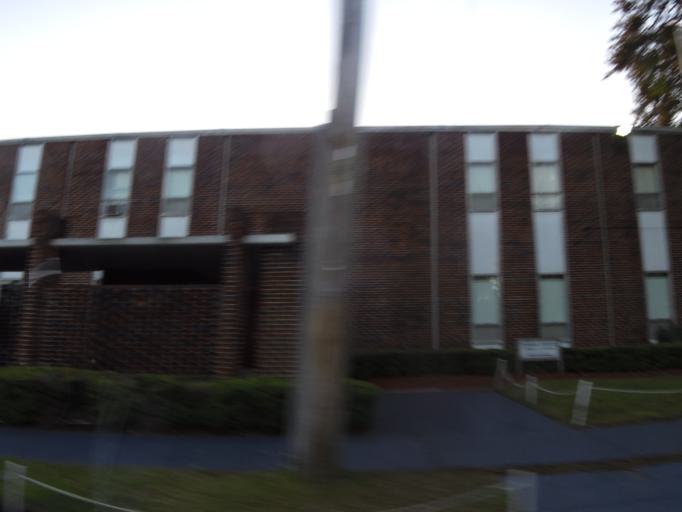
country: US
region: Florida
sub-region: Duval County
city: Jacksonville
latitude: 30.3356
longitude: -81.7167
